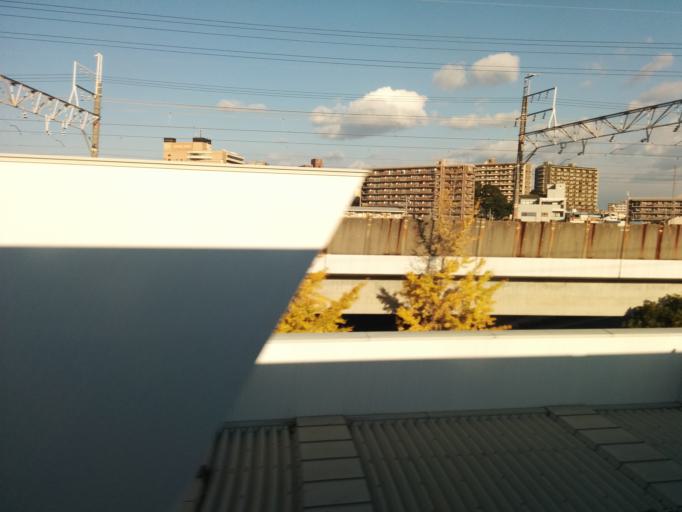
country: JP
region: Shizuoka
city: Hamamatsu
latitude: 34.6975
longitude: 137.7259
